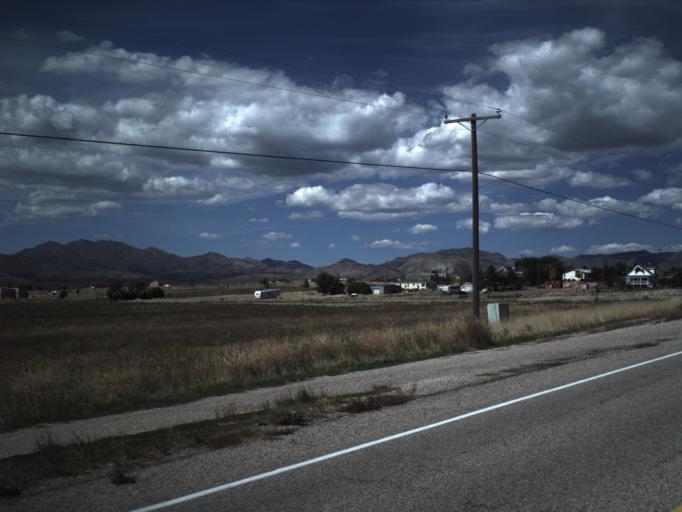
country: US
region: Utah
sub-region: Washington County
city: Ivins
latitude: 37.3346
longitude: -113.6932
